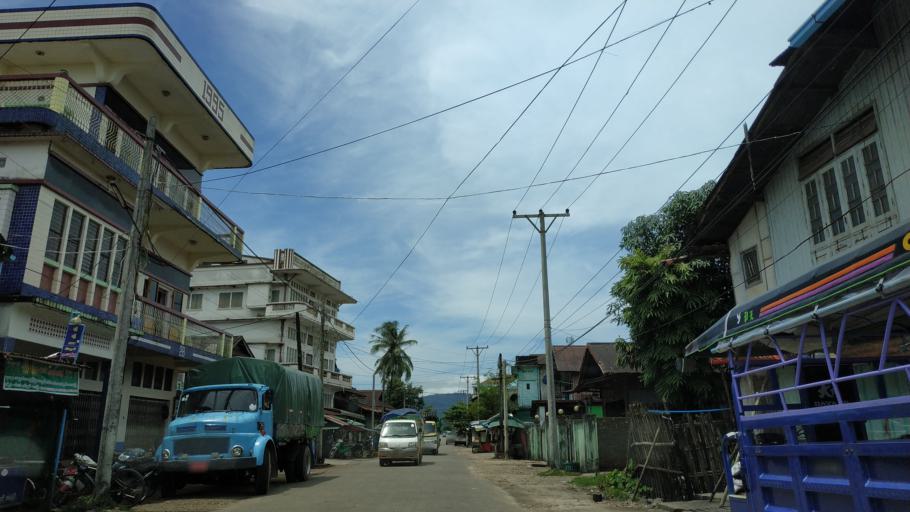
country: MM
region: Tanintharyi
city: Dawei
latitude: 14.0707
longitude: 98.1894
